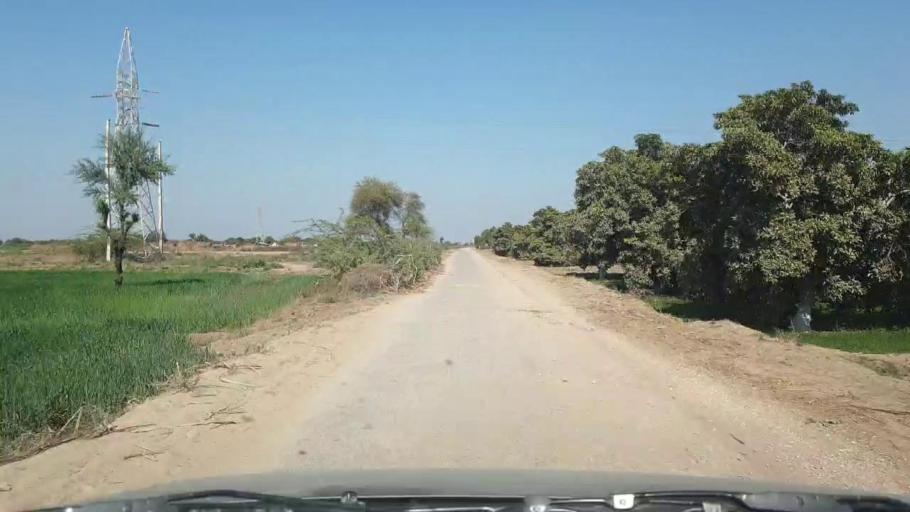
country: PK
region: Sindh
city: Samaro
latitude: 25.3003
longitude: 69.2654
